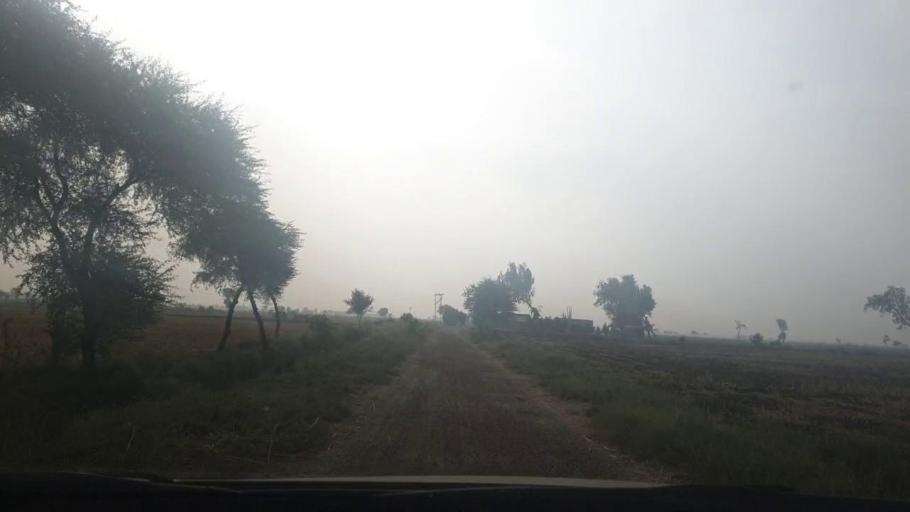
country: PK
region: Sindh
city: Tando Muhammad Khan
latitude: 25.1082
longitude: 68.5225
